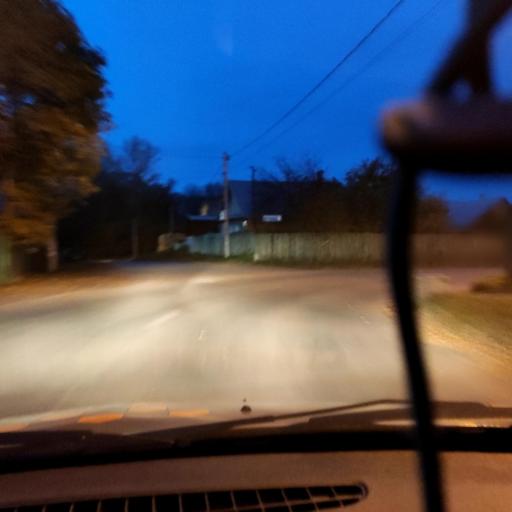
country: RU
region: Bashkortostan
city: Ufa
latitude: 54.7261
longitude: 55.9103
